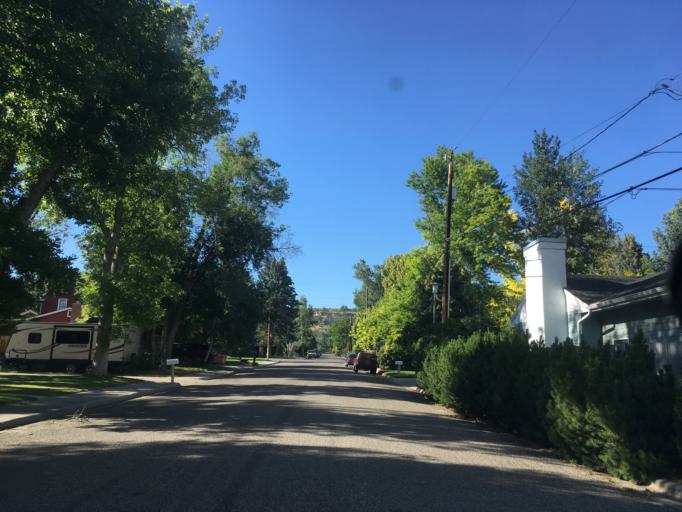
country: US
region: Montana
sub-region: Yellowstone County
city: Billings
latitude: 45.7941
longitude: -108.5642
